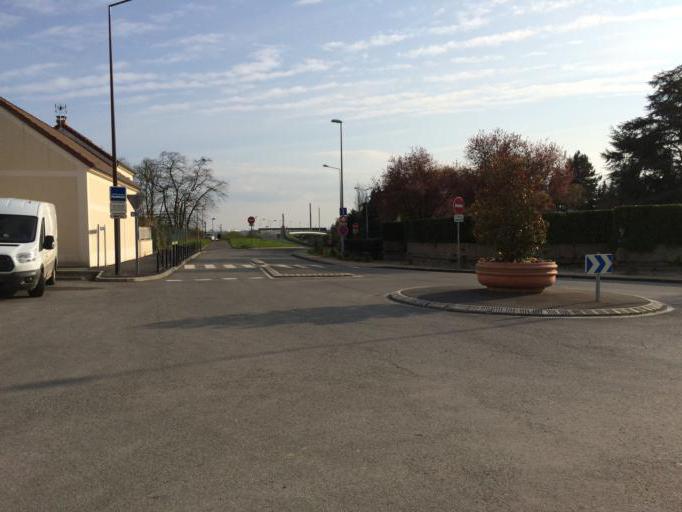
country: FR
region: Ile-de-France
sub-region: Departement de l'Essonne
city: Fleury-Merogis
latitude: 48.6278
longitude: 2.3615
